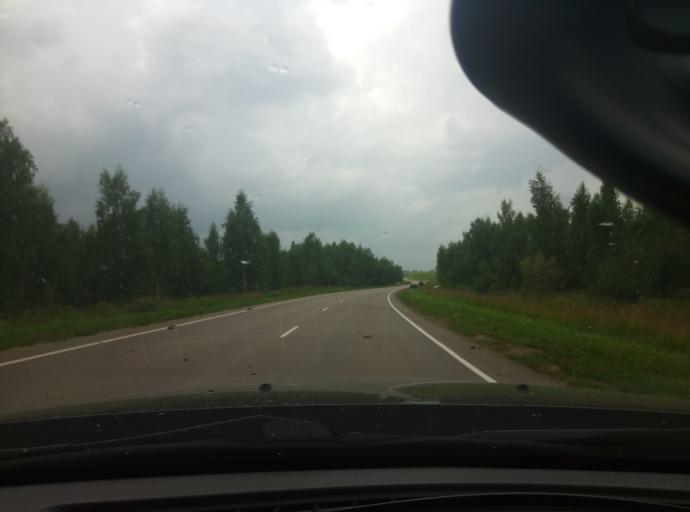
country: RU
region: Tula
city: Lomintsevskiy
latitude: 53.9376
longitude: 37.6151
